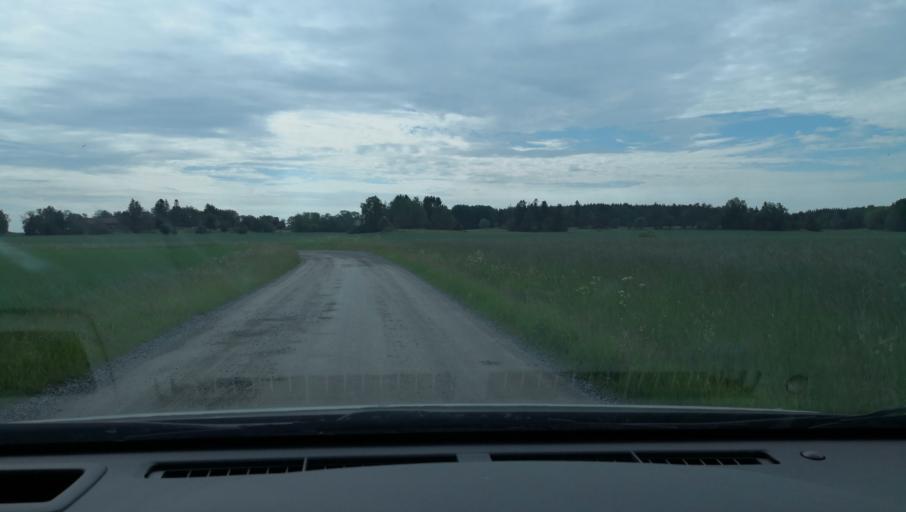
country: SE
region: Uppsala
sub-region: Enkopings Kommun
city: Enkoping
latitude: 59.7054
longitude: 17.1516
